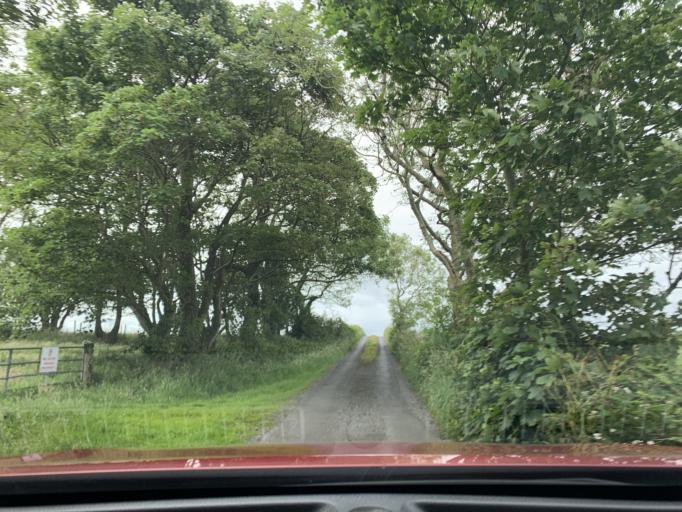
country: IE
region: Connaught
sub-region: Sligo
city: Sligo
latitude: 54.3661
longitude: -8.5209
